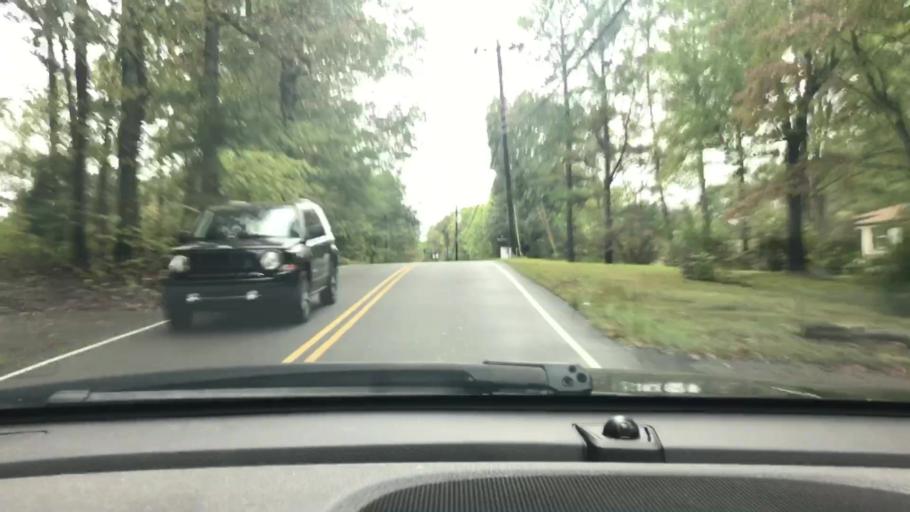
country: US
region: Tennessee
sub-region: Cheatham County
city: Kingston Springs
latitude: 36.1079
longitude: -87.1383
